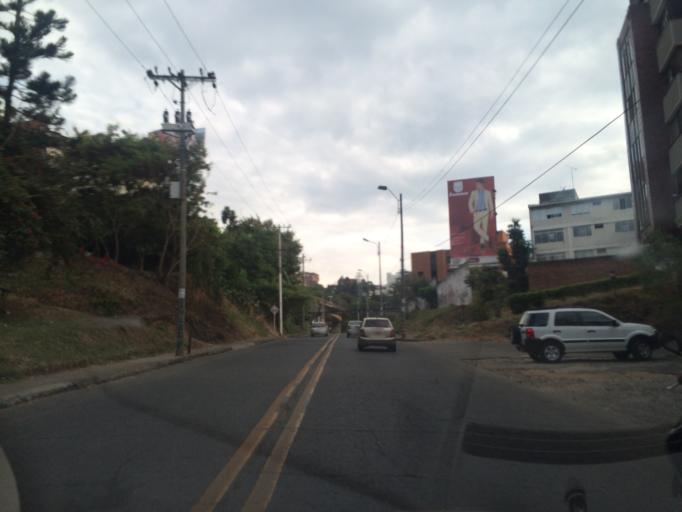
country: CO
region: Valle del Cauca
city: Cali
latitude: 3.4418
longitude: -76.5481
